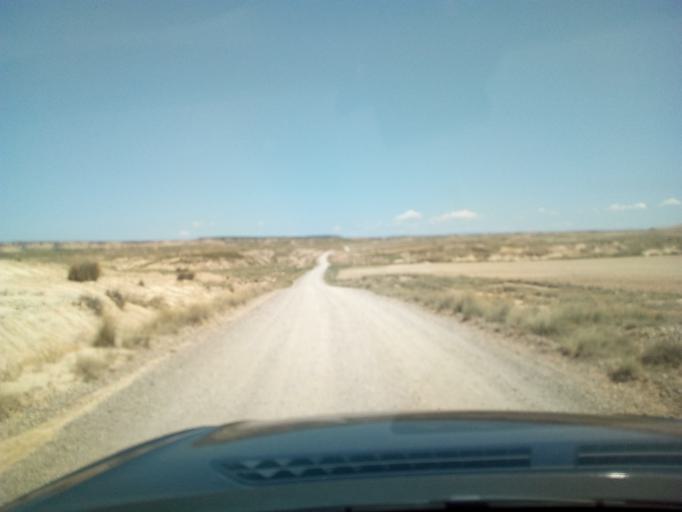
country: ES
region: Navarre
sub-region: Provincia de Navarra
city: Fustinana
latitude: 42.1648
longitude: -1.4288
